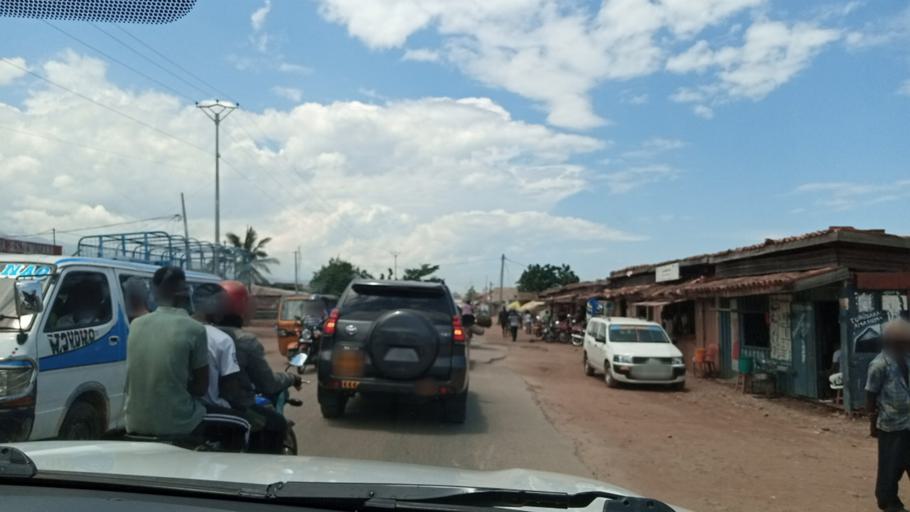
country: BI
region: Bujumbura Mairie
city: Bujumbura
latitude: -3.4316
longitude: 29.3544
